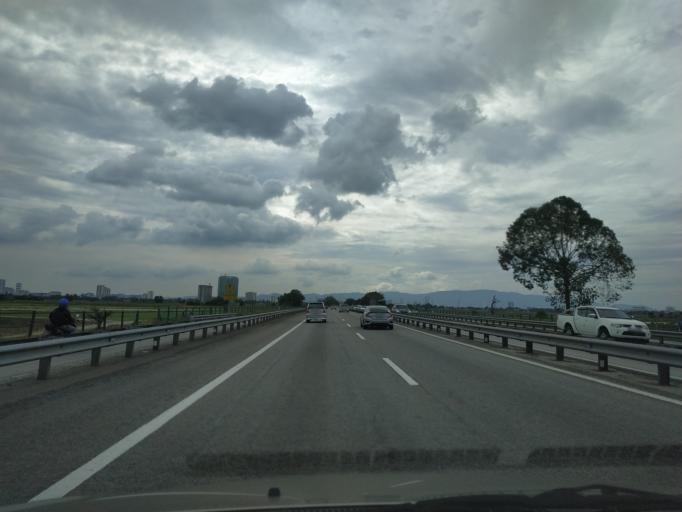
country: MY
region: Penang
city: Bukit Mertajam
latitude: 5.4009
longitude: 100.4367
